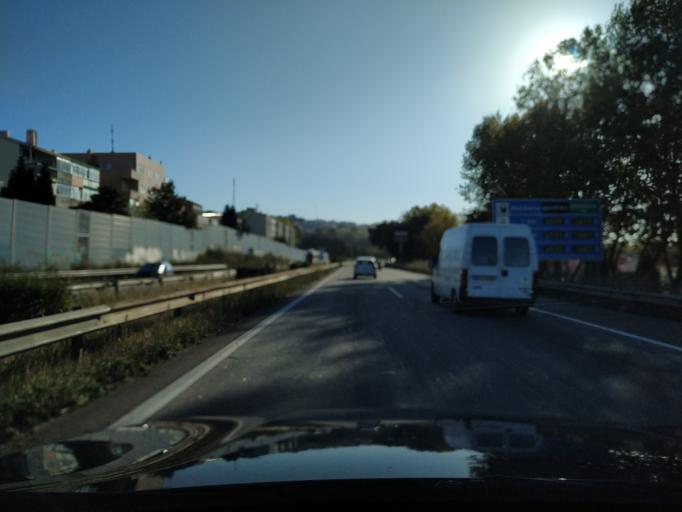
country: PT
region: Porto
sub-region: Vila Nova de Gaia
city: Vilar de Andorinho
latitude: 41.1120
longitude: -8.6123
